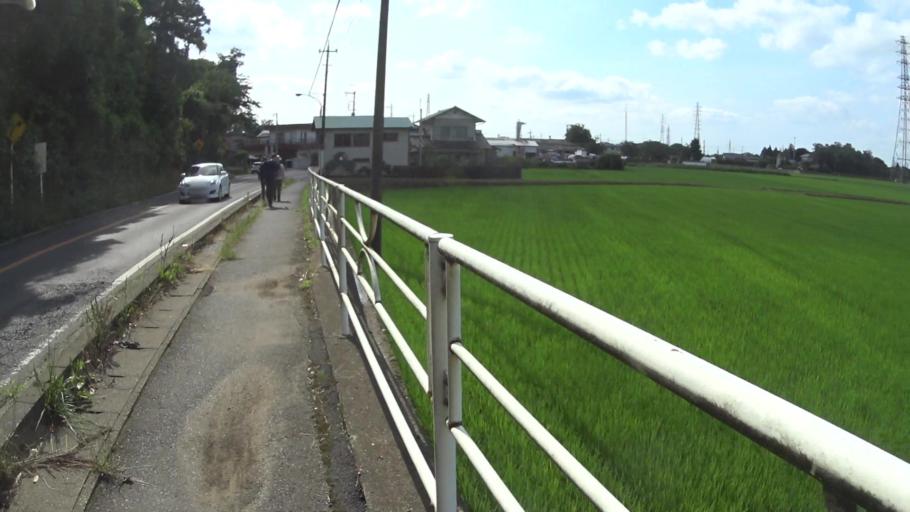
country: JP
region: Chiba
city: Sawara
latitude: 35.8857
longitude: 140.5159
